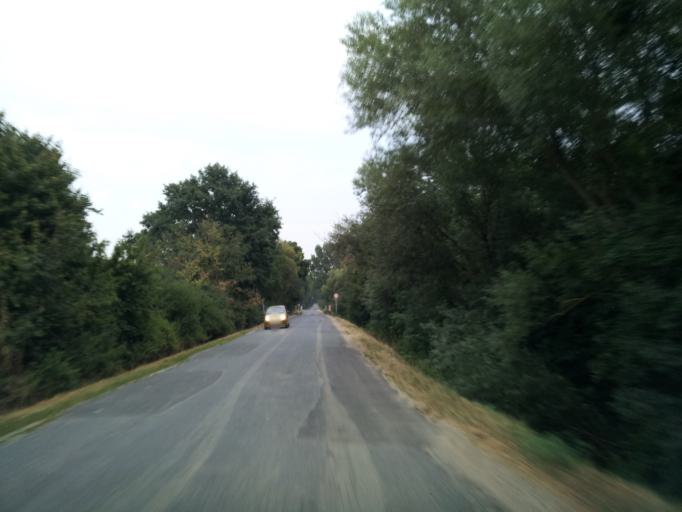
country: HU
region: Vas
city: Sarvar
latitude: 47.2057
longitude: 16.9313
